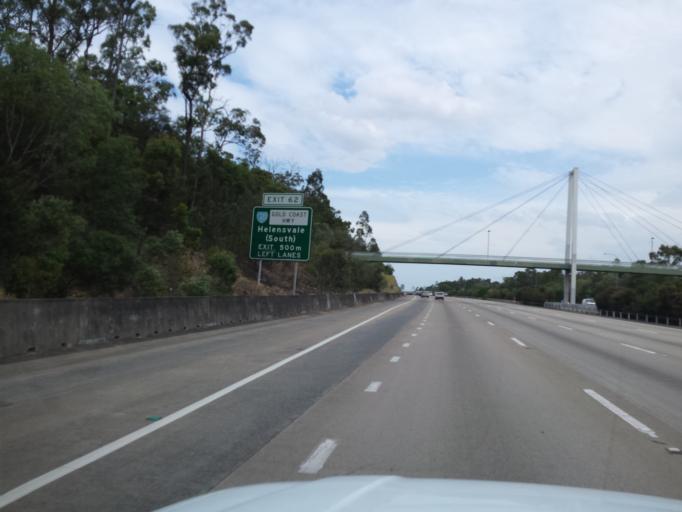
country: AU
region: Queensland
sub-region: Gold Coast
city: Upper Coomera
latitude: -27.9199
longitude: 153.3235
